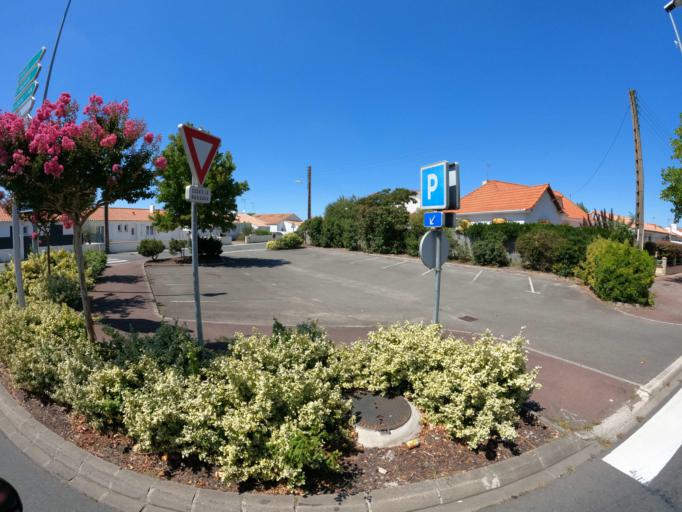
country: FR
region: Pays de la Loire
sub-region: Departement de la Vendee
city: Challans
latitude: 46.8398
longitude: -1.8654
